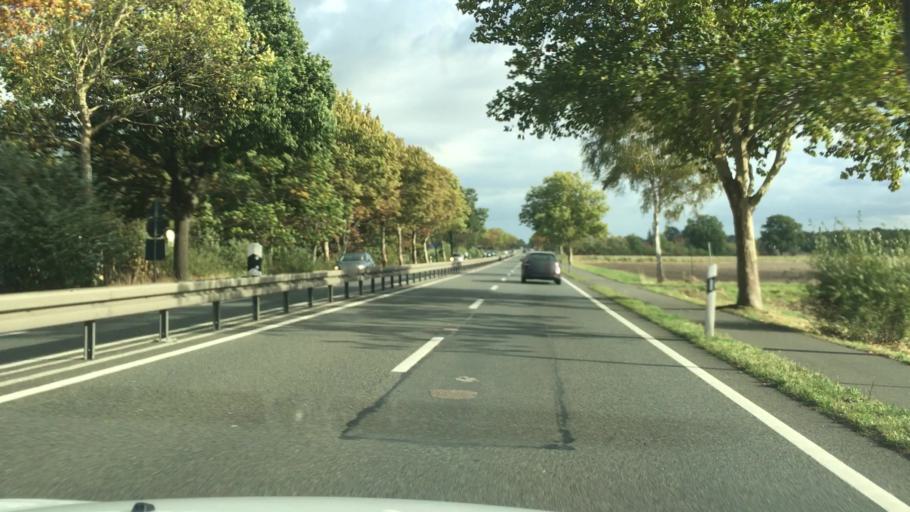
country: DE
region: Lower Saxony
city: Garbsen
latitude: 52.4518
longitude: 9.5575
